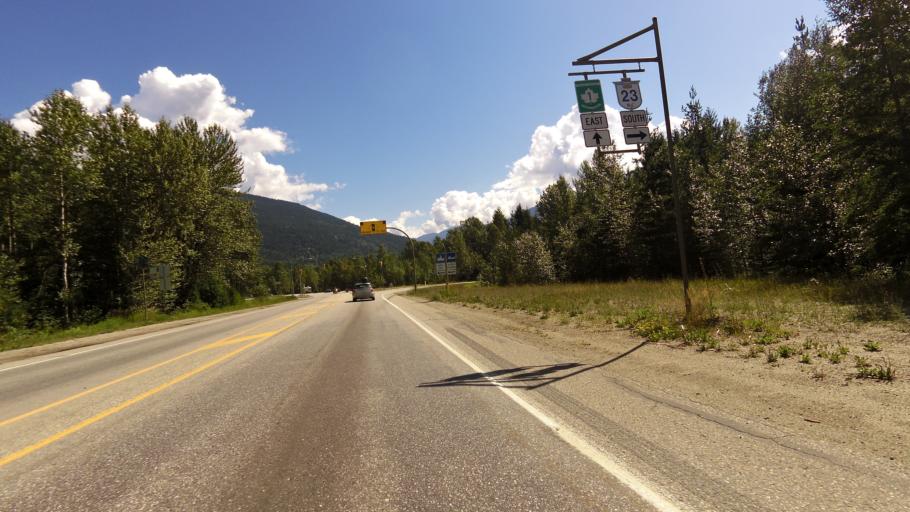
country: CA
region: British Columbia
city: Revelstoke
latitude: 51.0030
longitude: -118.2276
